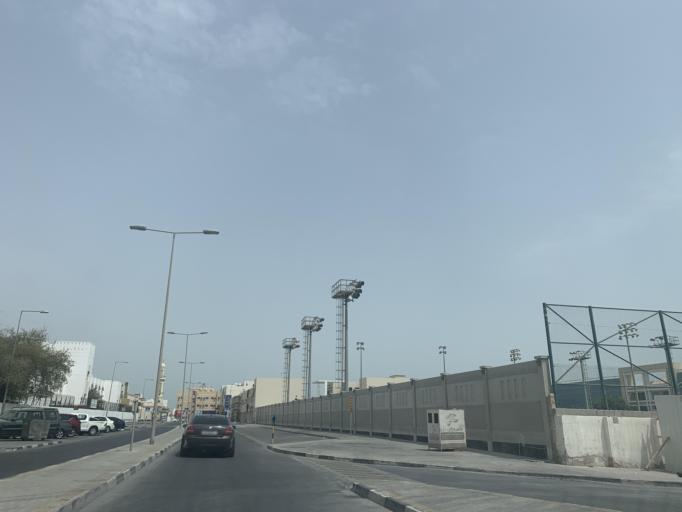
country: BH
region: Northern
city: Ar Rifa'
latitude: 26.1281
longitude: 50.5731
